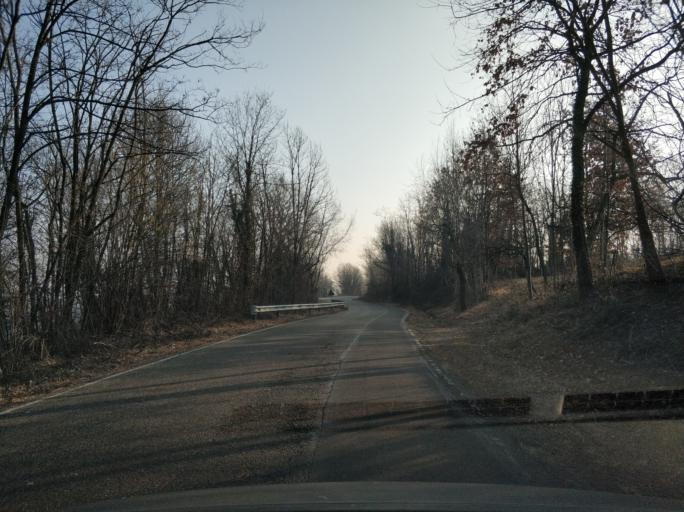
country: IT
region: Piedmont
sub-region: Provincia di Torino
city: Barbania
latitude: 45.2834
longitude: 7.6287
